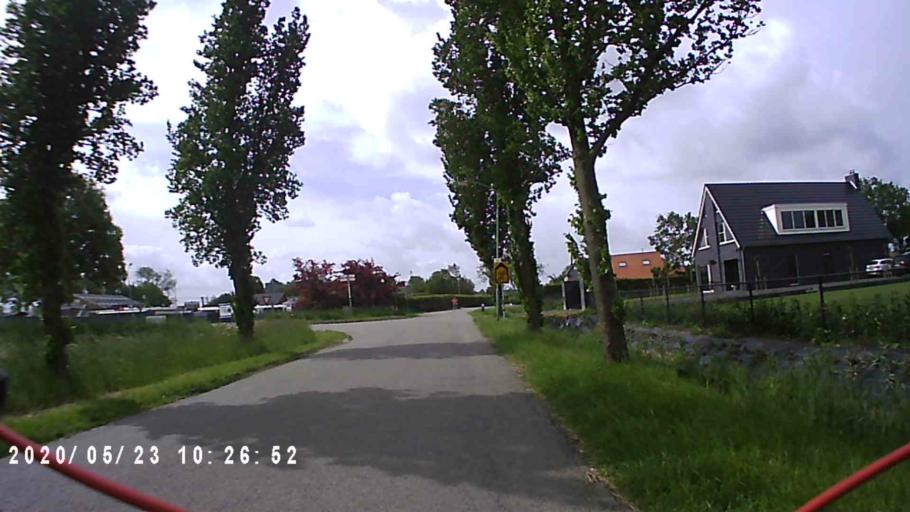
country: NL
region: Groningen
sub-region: Gemeente Appingedam
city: Appingedam
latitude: 53.3018
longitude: 6.8520
